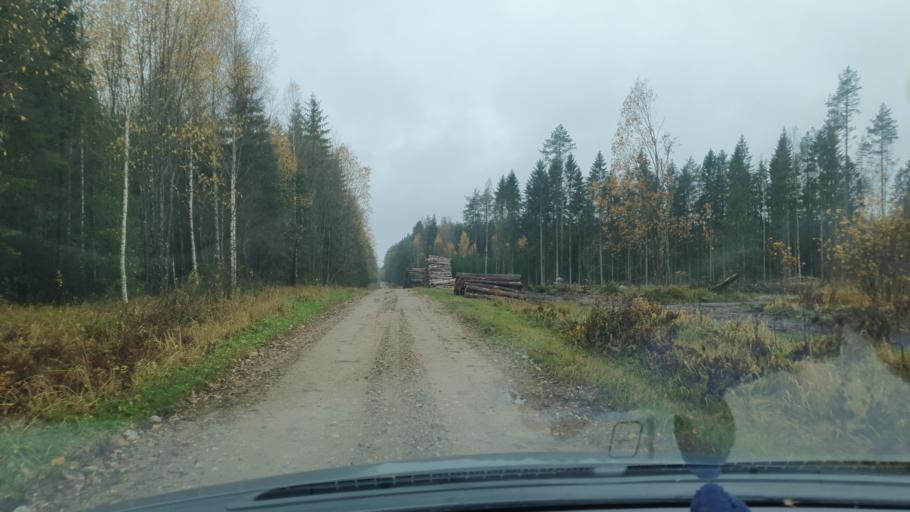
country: EE
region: Viljandimaa
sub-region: Karksi vald
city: Karksi-Nuia
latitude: 57.9819
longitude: 25.6322
